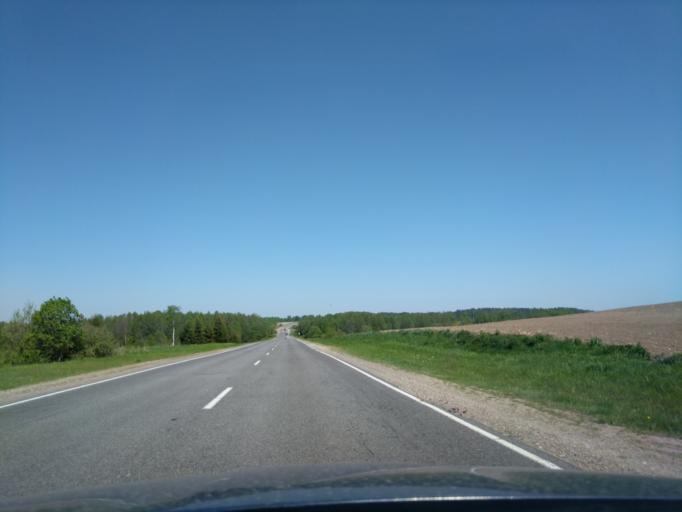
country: BY
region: Minsk
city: Il'ya
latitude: 54.2947
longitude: 27.4823
